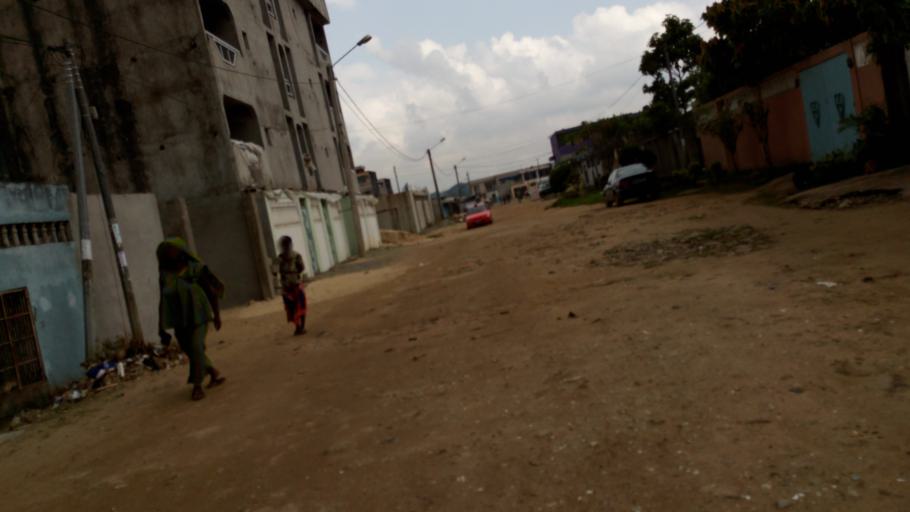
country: CI
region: Lagunes
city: Abobo
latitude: 5.3988
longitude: -4.0052
